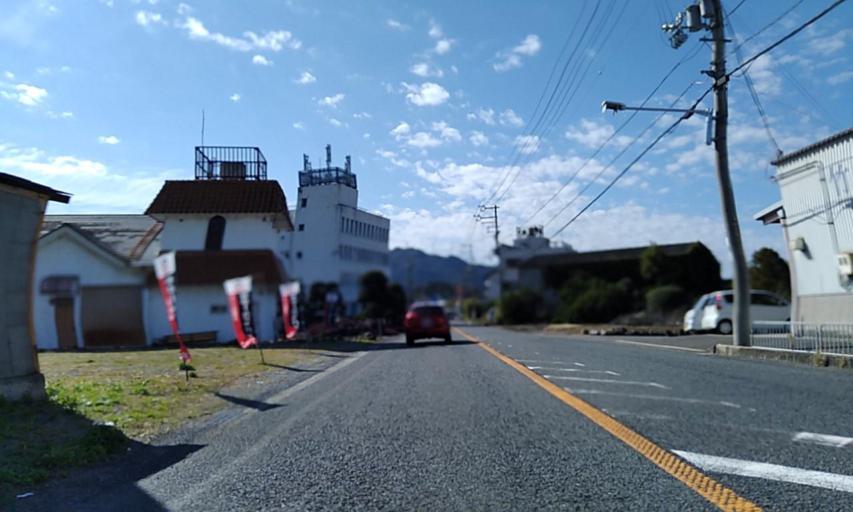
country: JP
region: Wakayama
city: Kainan
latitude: 34.0249
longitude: 135.1808
